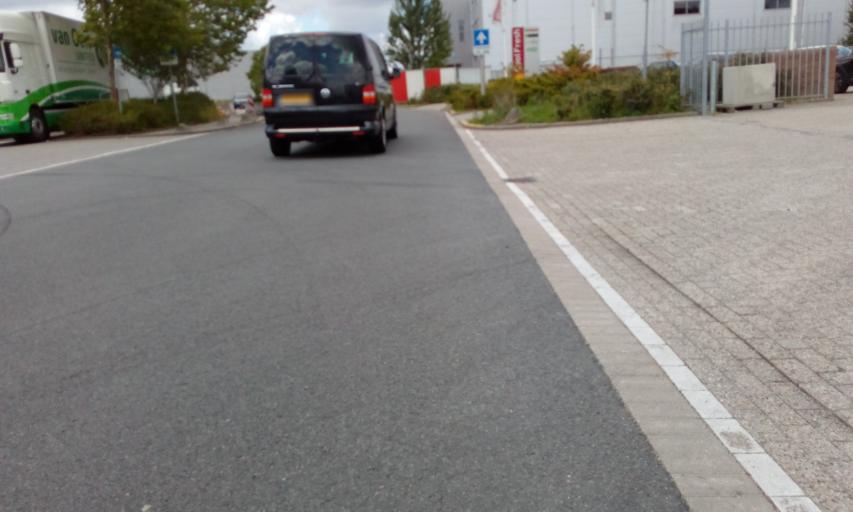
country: NL
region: South Holland
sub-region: Gemeente Zwijndrecht
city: Heerjansdam
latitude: 51.8598
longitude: 4.5622
